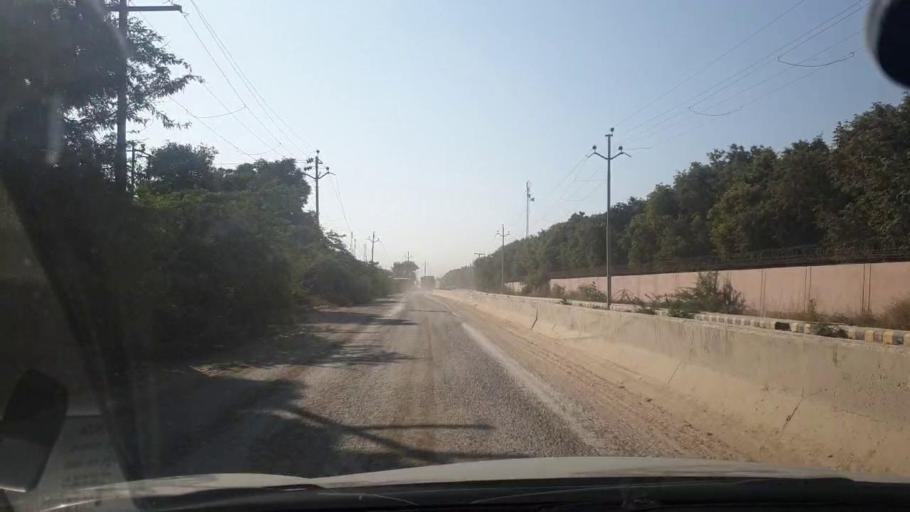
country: PK
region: Sindh
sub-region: Karachi District
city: Karachi
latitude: 25.0863
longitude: 67.0124
